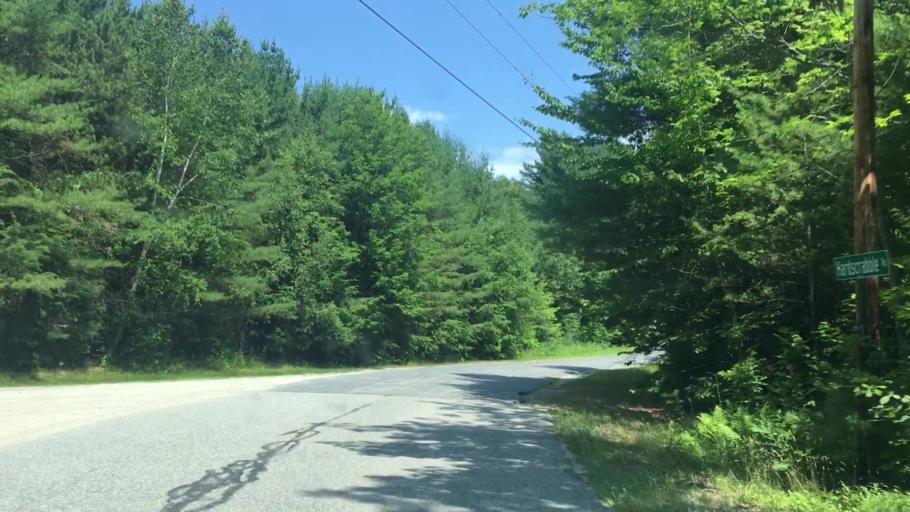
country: US
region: Maine
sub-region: Kennebec County
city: Wayne
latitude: 44.3188
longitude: -70.0585
